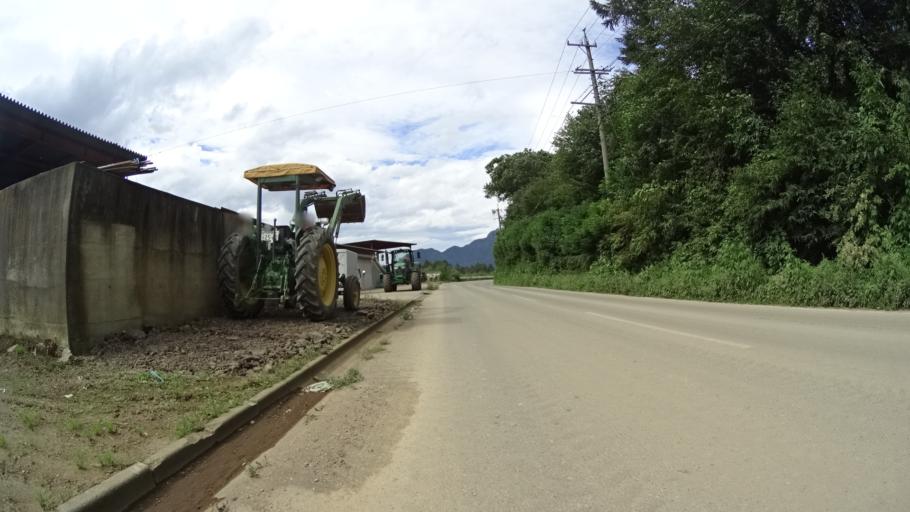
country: JP
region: Yamanashi
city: Nirasaki
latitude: 35.9418
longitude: 138.5479
